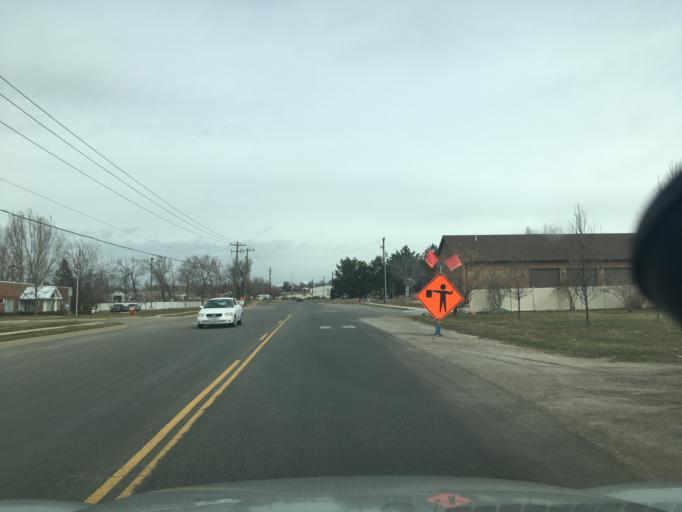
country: US
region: Utah
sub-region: Davis County
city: Layton
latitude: 41.0865
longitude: -111.9591
